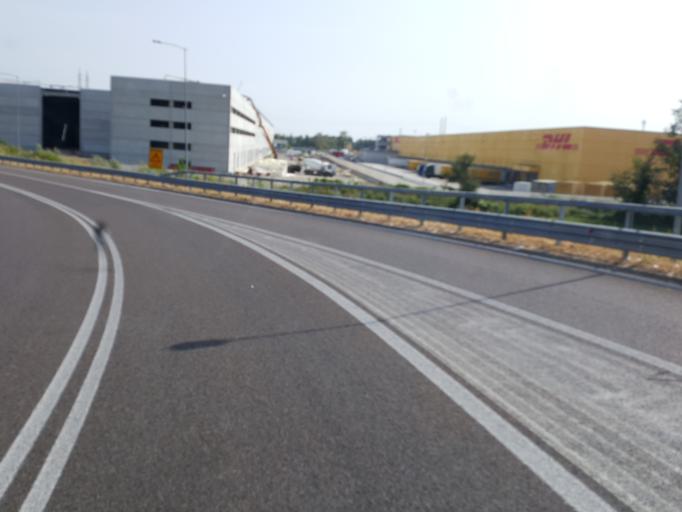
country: IT
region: Lombardy
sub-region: Citta metropolitana di Milano
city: Melzo
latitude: 45.5135
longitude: 9.4317
